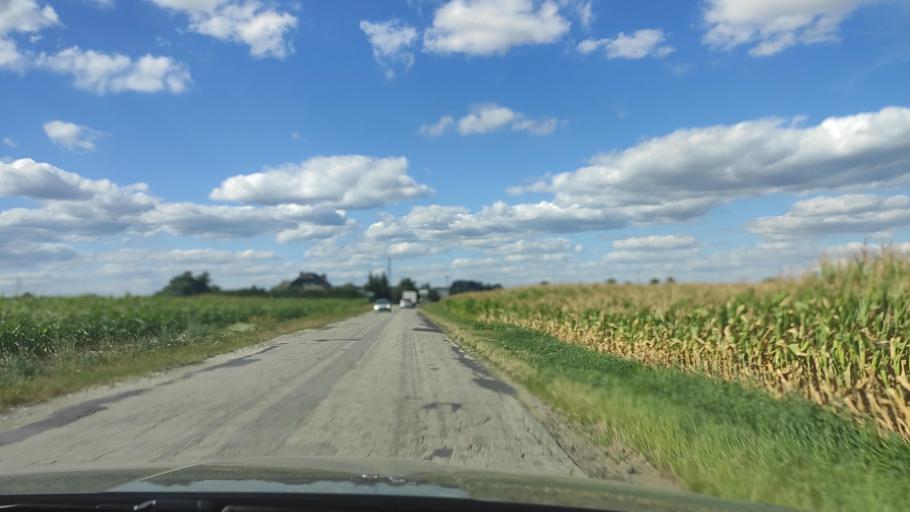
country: PL
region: Greater Poland Voivodeship
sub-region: Powiat poznanski
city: Kleszczewo
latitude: 52.3728
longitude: 17.1672
